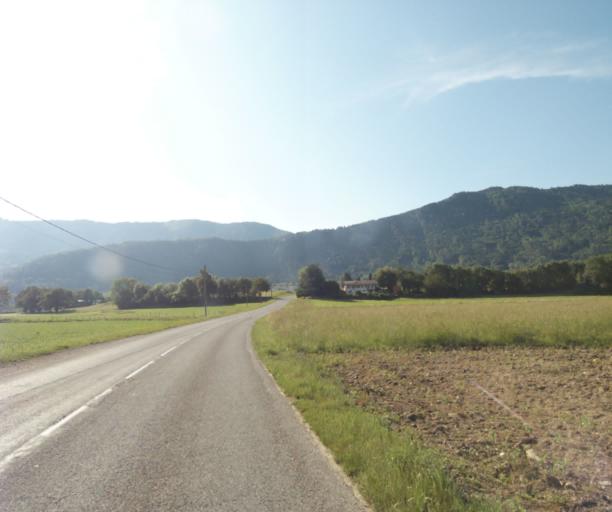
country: FR
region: Rhone-Alpes
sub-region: Departement de la Haute-Savoie
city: Allinges
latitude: 46.3176
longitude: 6.4809
